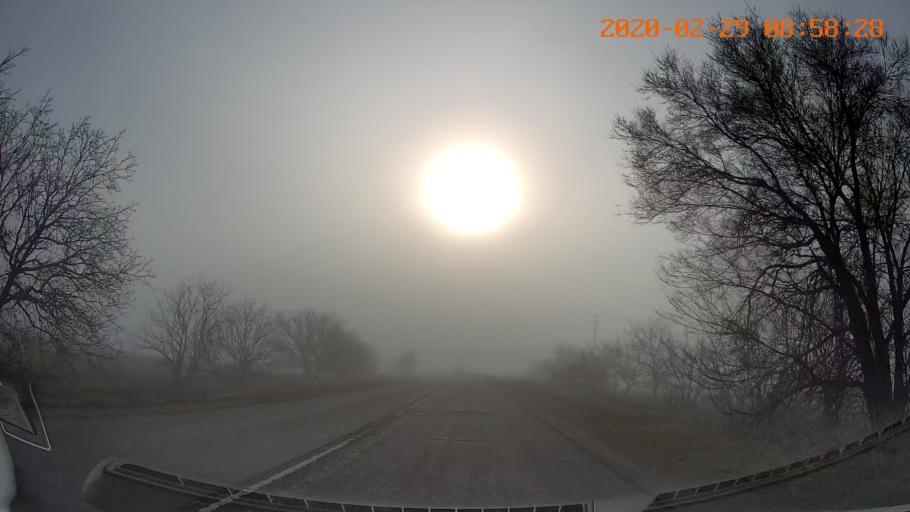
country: MD
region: Telenesti
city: Tiraspolul Nou
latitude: 46.9206
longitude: 29.6413
